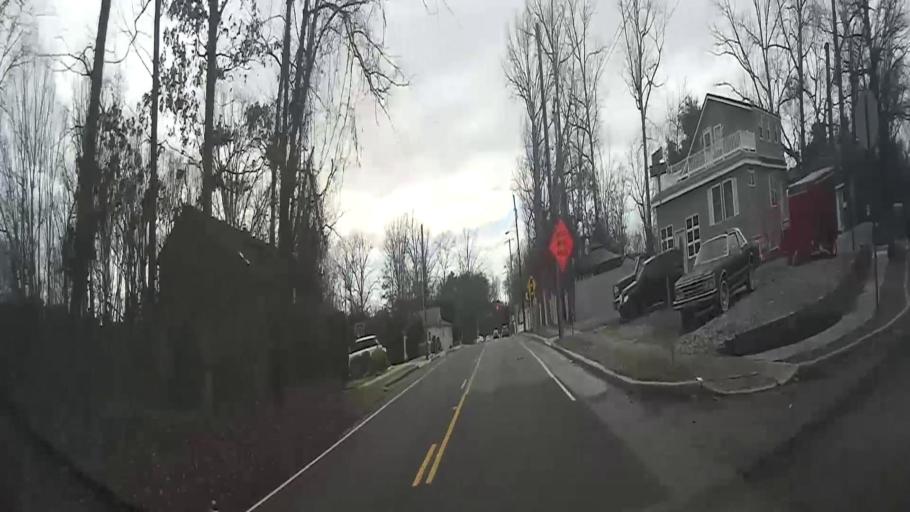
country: US
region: New Jersey
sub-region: Camden County
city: Pine Hill
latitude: 39.7792
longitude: -74.9950
